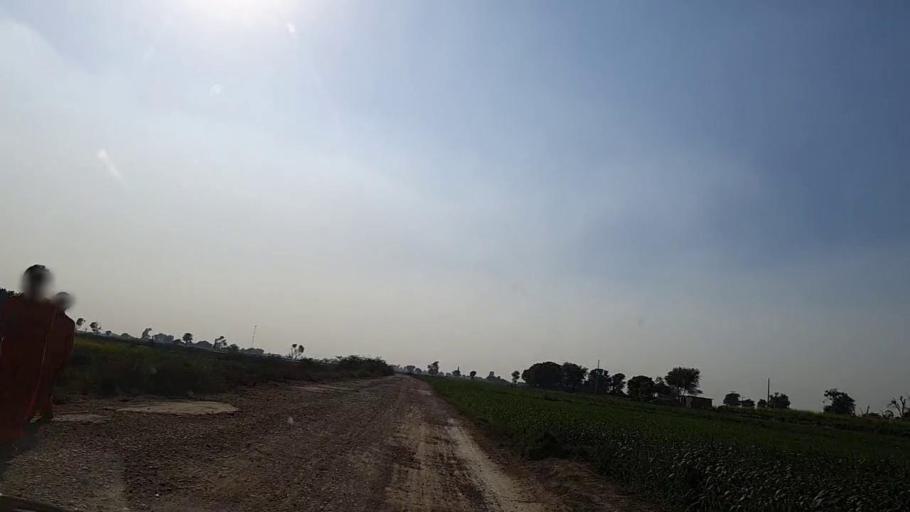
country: PK
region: Sindh
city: Sakrand
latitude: 26.1241
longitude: 68.2501
